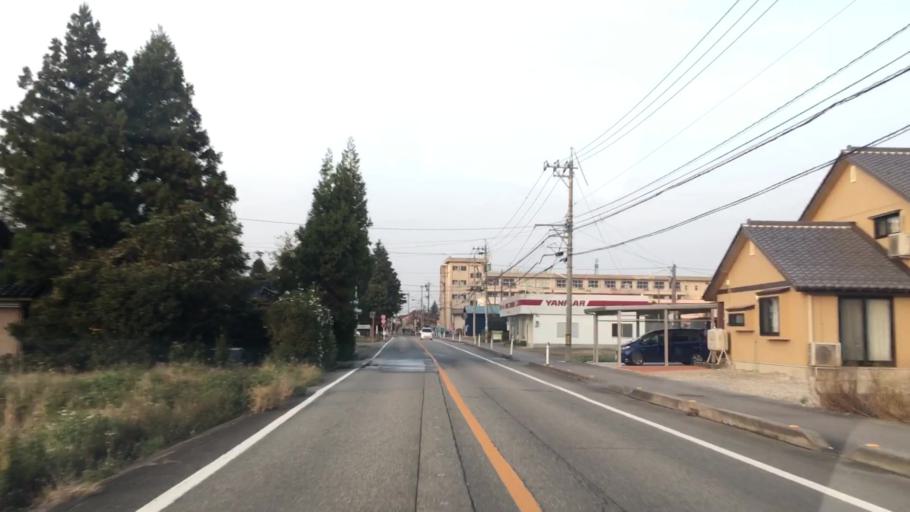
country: JP
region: Toyama
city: Toyama-shi
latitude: 36.6206
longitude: 137.2518
